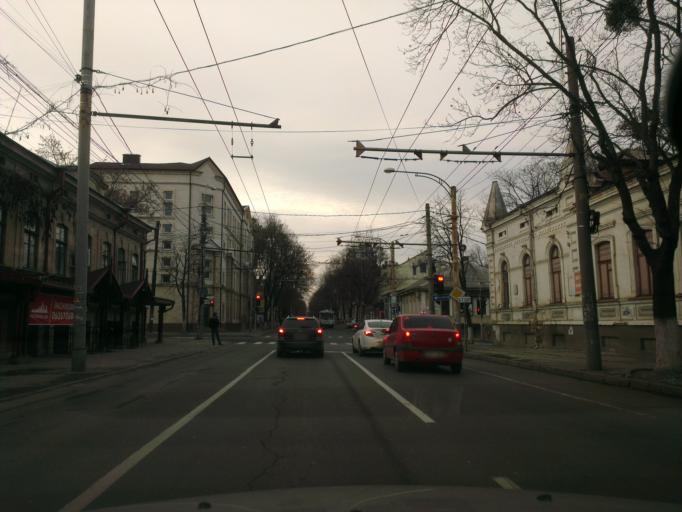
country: MD
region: Chisinau
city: Chisinau
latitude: 47.0223
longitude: 28.8271
